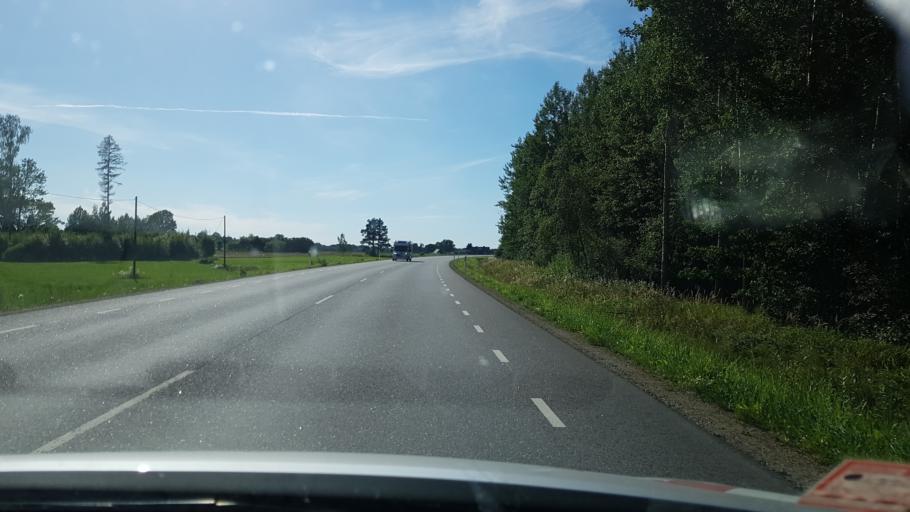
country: EE
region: Tartu
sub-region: UElenurme vald
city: Ulenurme
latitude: 58.1767
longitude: 26.8689
